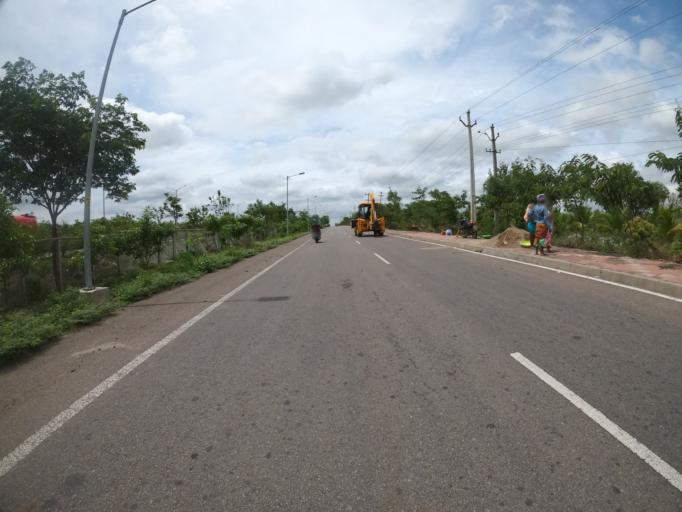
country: IN
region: Telangana
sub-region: Hyderabad
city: Hyderabad
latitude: 17.2915
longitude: 78.3809
